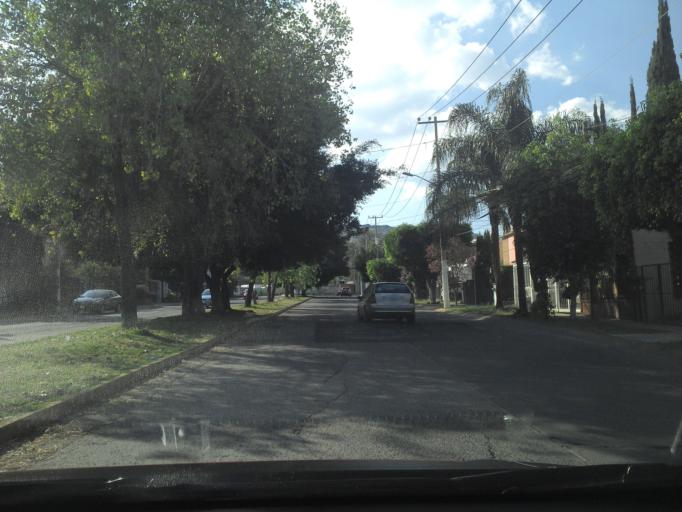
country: MX
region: Jalisco
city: Guadalajara
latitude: 20.6526
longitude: -103.4421
